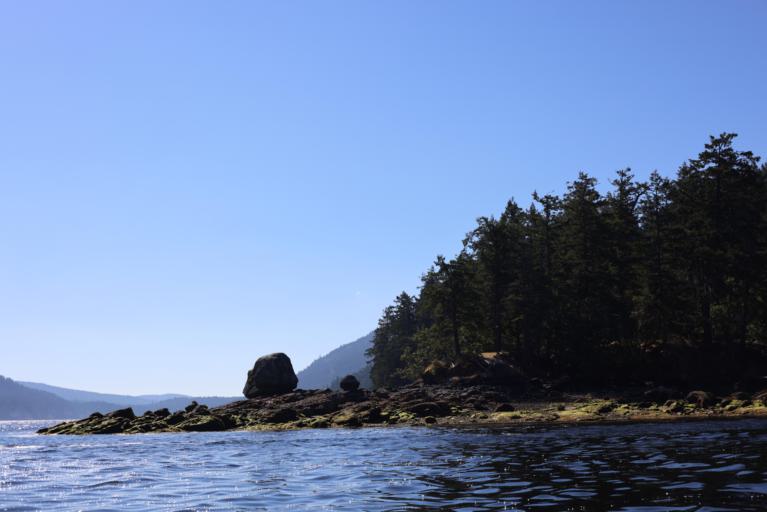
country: CA
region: British Columbia
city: North Cowichan
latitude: 48.8090
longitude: -123.5899
